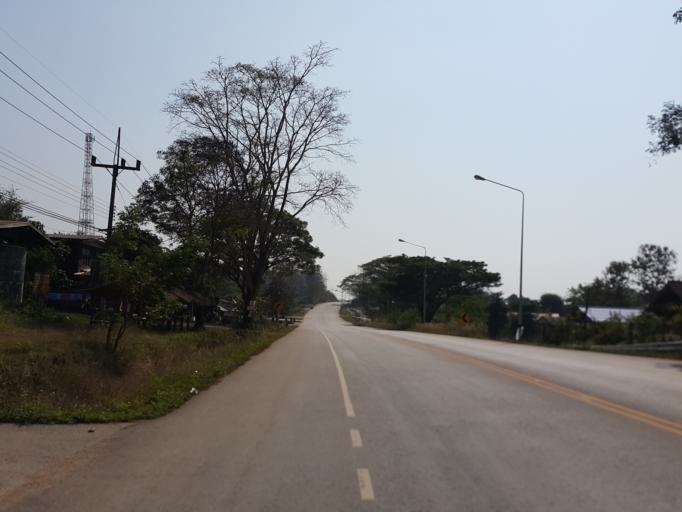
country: TH
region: Lampang
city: Mueang Pan
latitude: 18.9075
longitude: 99.6067
